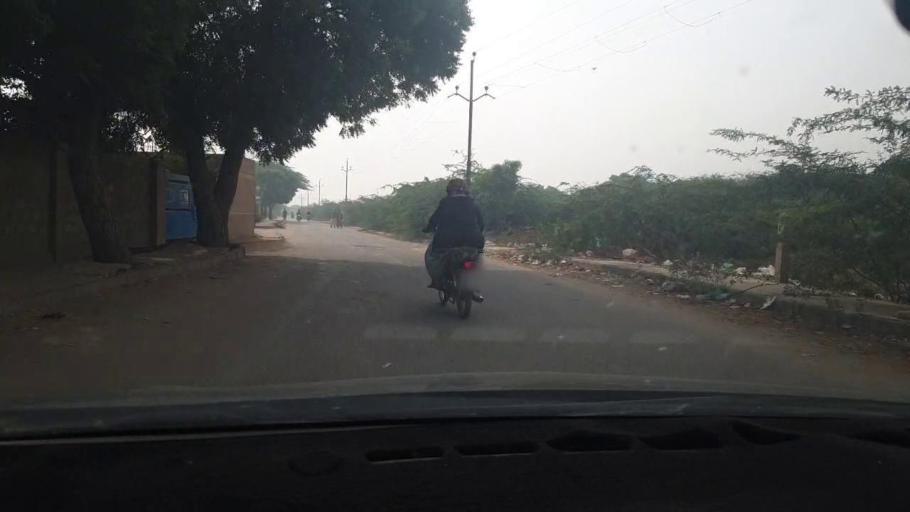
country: PK
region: Sindh
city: Malir Cantonment
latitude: 24.9378
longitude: 67.3342
